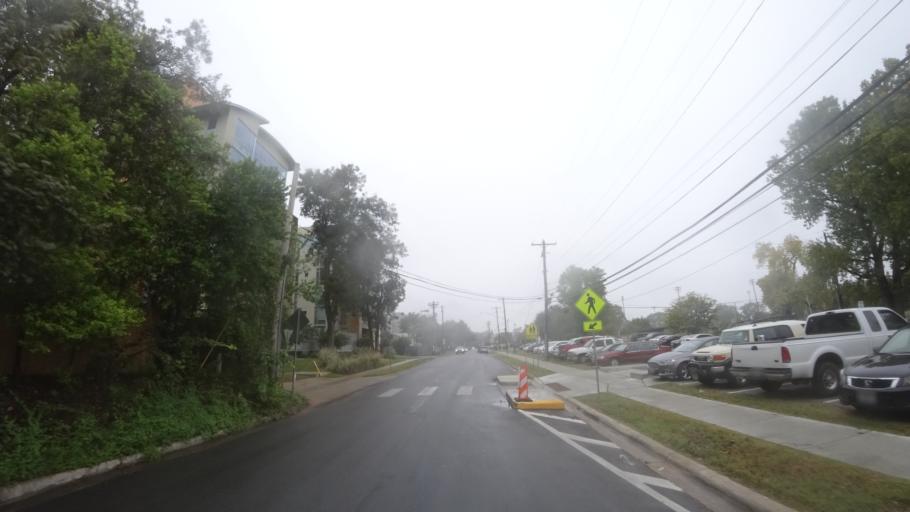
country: US
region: Texas
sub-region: Travis County
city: Austin
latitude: 30.2640
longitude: -97.7598
